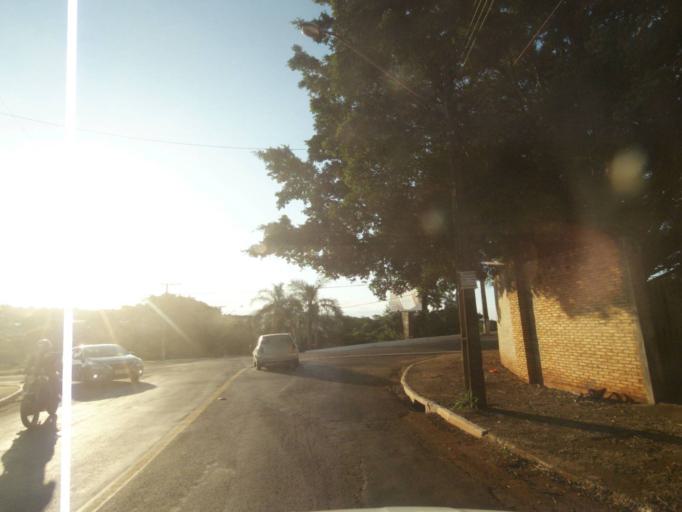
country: BR
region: Parana
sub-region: Londrina
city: Londrina
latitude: -23.3471
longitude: -51.1951
